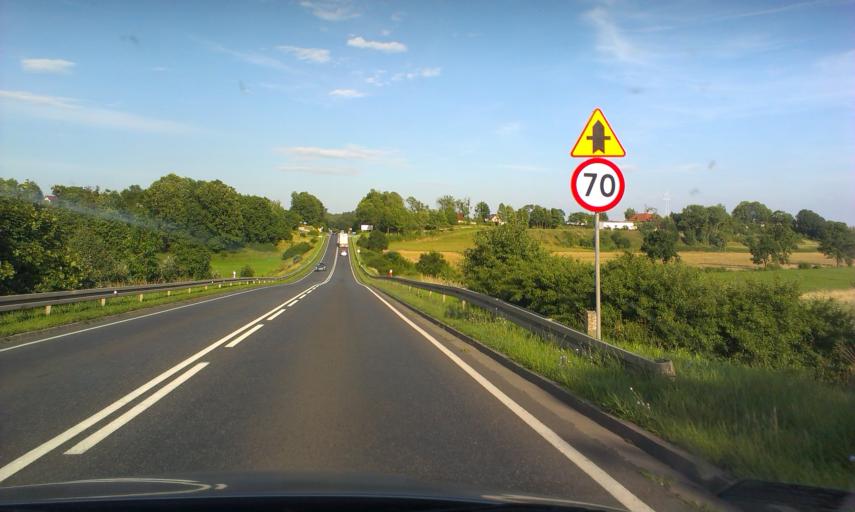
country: PL
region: Kujawsko-Pomorskie
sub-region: Powiat bydgoski
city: Sicienko
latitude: 53.1572
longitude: 17.8568
